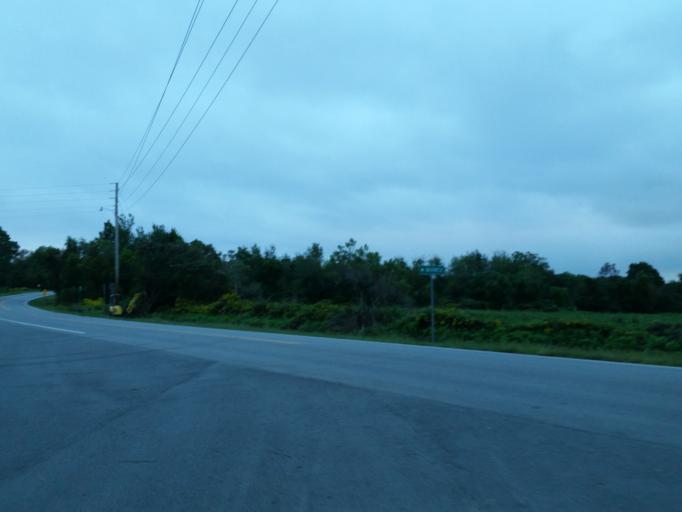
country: US
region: Georgia
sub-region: Crisp County
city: Cordele
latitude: 31.8374
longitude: -83.7431
